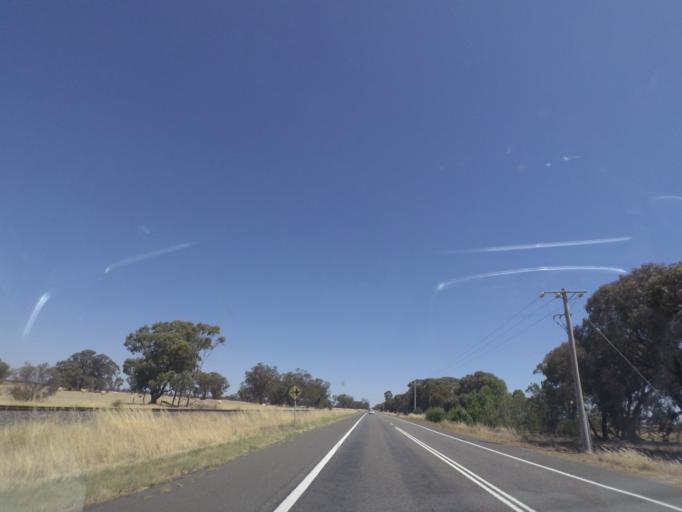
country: AU
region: Victoria
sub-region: Greater Shepparton
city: Shepparton
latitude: -36.1963
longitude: 145.4318
